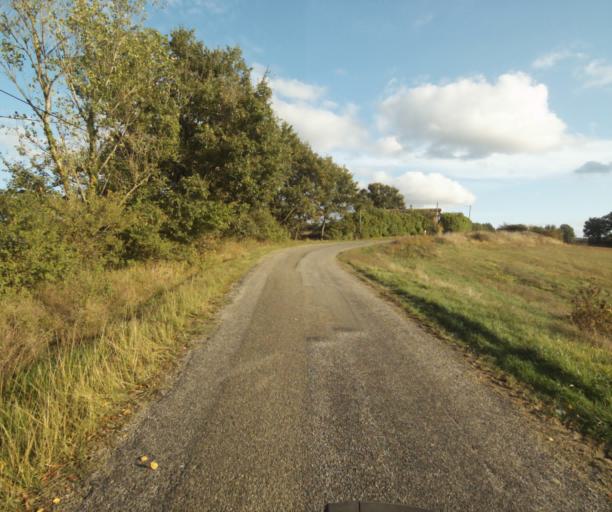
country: FR
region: Midi-Pyrenees
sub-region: Departement de la Haute-Garonne
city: Launac
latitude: 43.8190
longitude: 1.1347
